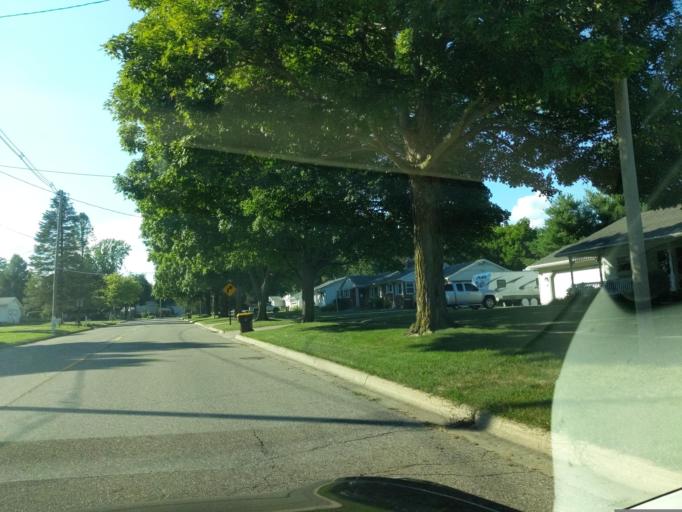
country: US
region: Michigan
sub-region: Ingham County
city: Mason
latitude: 42.5737
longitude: -84.4466
